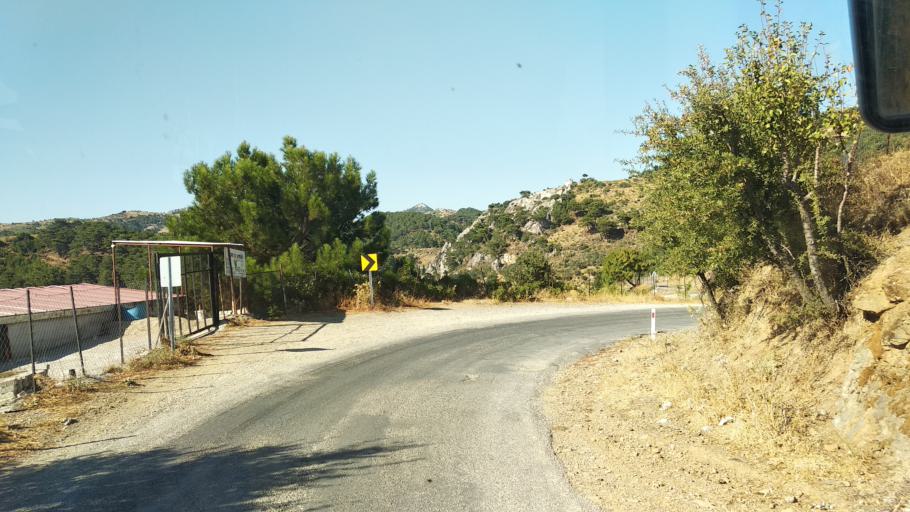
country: TR
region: Izmir
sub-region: Seferihisar
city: Seferhisar
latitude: 38.3144
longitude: 26.9548
